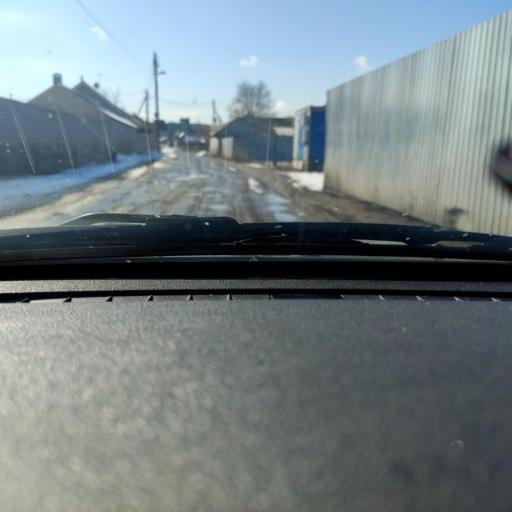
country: RU
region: Voronezj
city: Somovo
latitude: 51.7521
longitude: 39.3321
